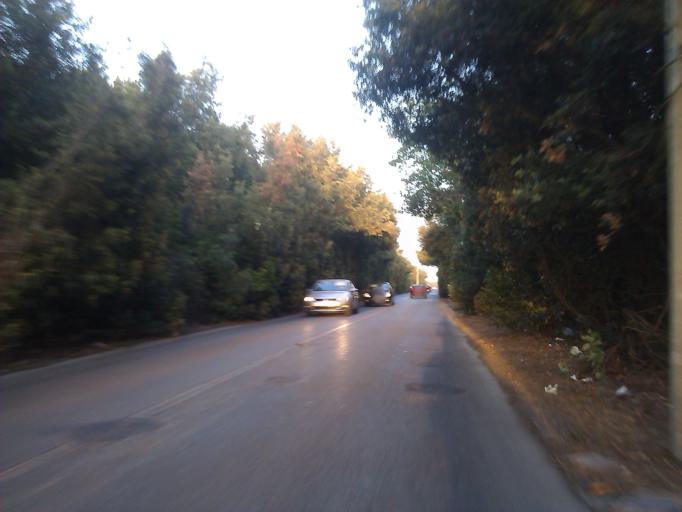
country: IT
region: Latium
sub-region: Citta metropolitana di Roma Capitale
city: Acilia-Castel Fusano-Ostia Antica
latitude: 41.7082
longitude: 12.3354
